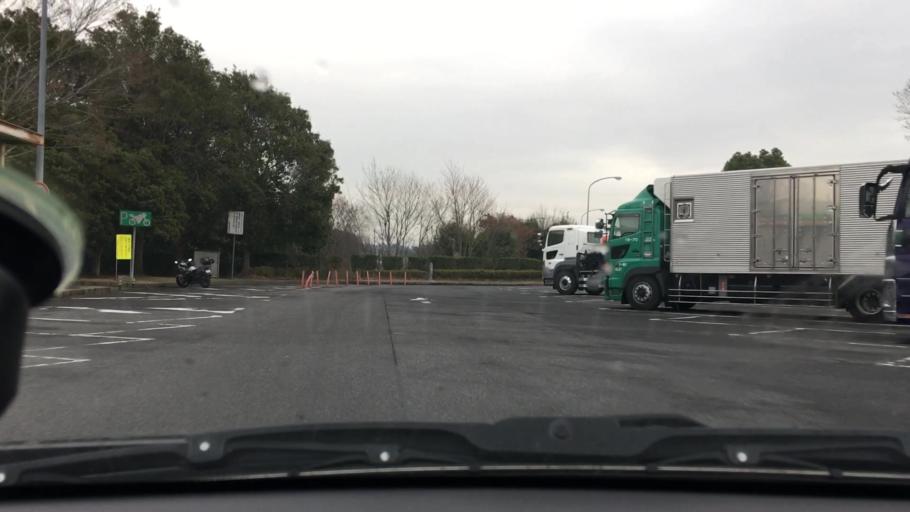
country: JP
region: Chiba
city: Narita
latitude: 35.8133
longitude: 140.4041
